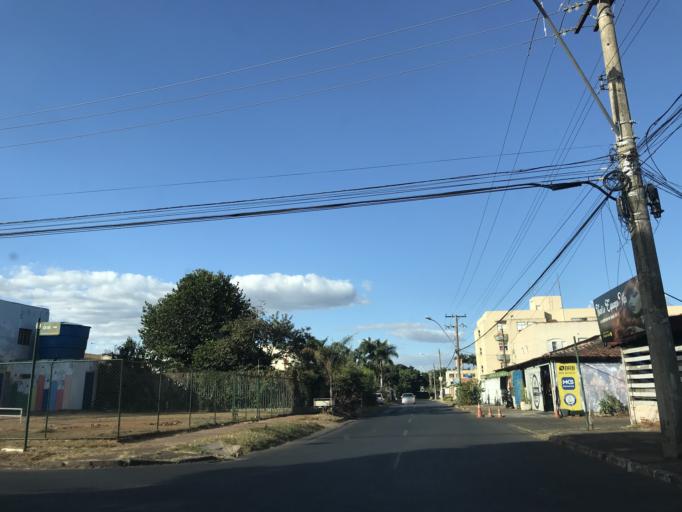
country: BR
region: Federal District
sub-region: Brasilia
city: Brasilia
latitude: -15.8154
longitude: -47.9880
